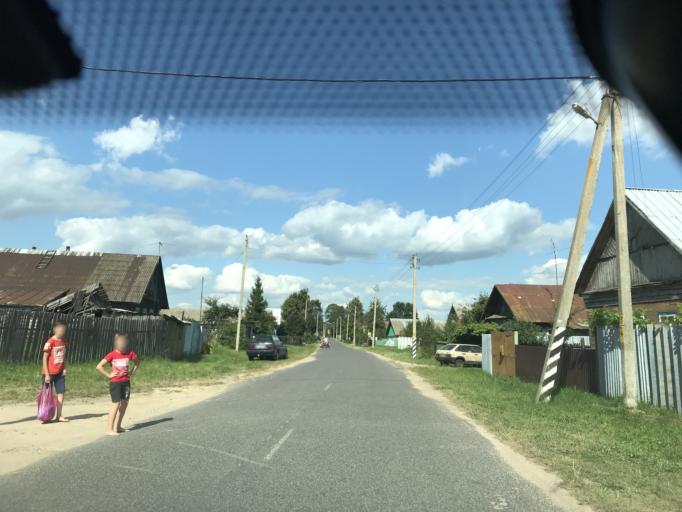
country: BY
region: Mogilev
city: Poselok Voskhod
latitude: 53.7842
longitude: 30.3518
